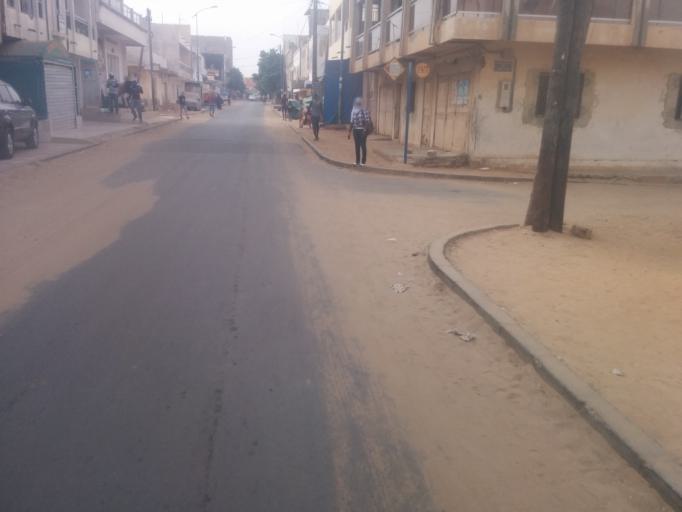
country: SN
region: Dakar
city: Grand Dakar
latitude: 14.7557
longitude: -17.4433
